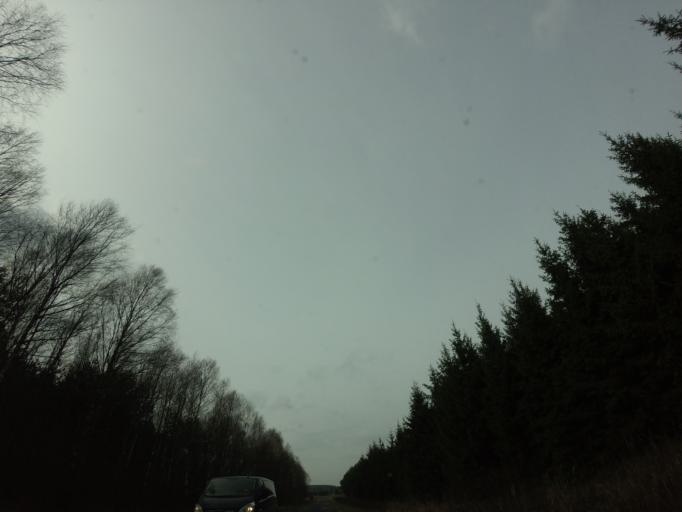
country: PL
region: West Pomeranian Voivodeship
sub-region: Powiat drawski
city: Wierzchowo
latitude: 53.4378
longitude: 16.1773
